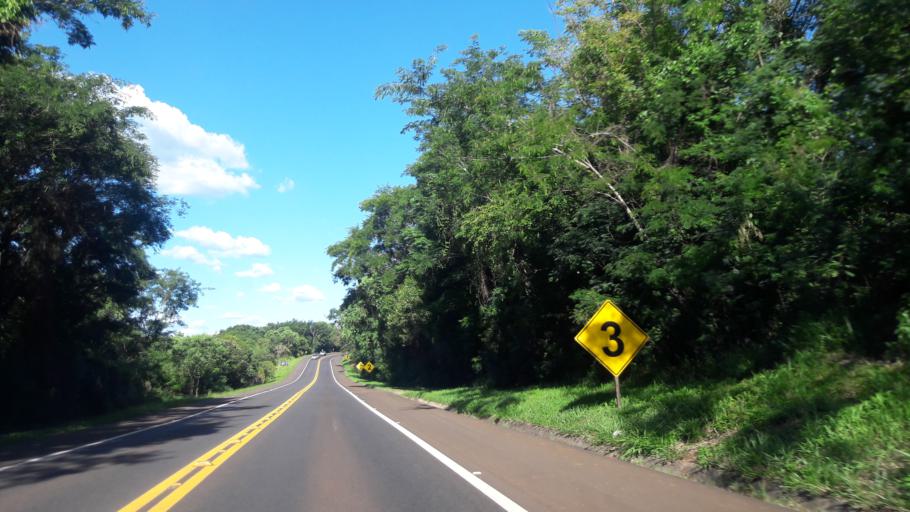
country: BR
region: Parana
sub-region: Laranjeiras Do Sul
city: Laranjeiras do Sul
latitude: -25.4202
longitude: -52.0373
